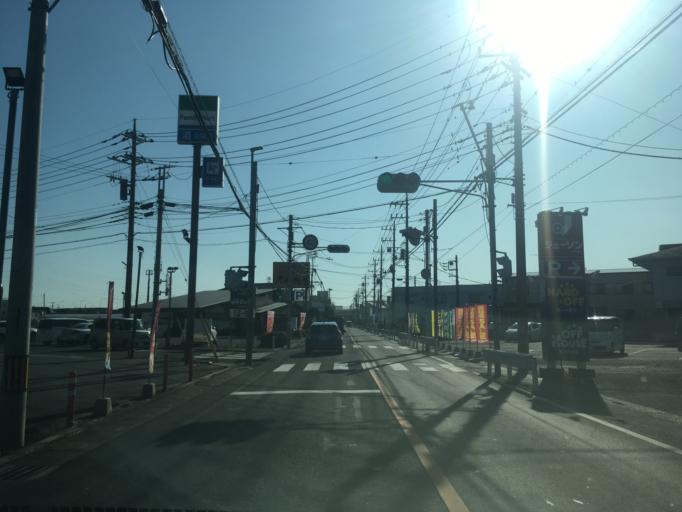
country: JP
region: Saitama
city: Kawagoe
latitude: 35.8843
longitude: 139.4764
